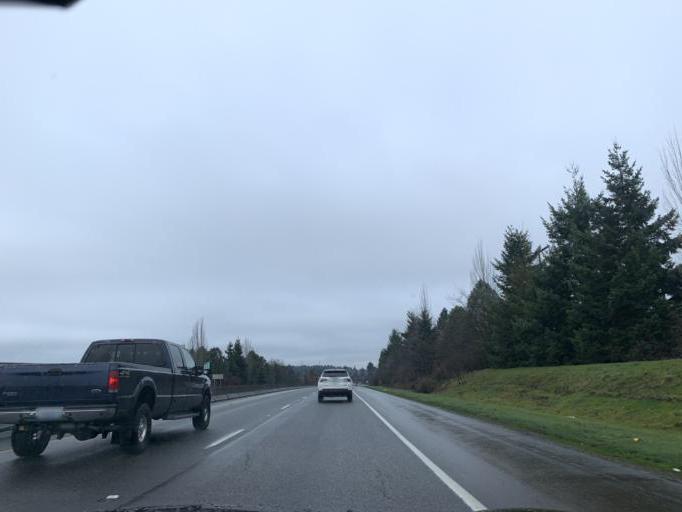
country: US
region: Washington
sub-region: Clark County
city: Orchards
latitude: 45.6822
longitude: -122.5549
